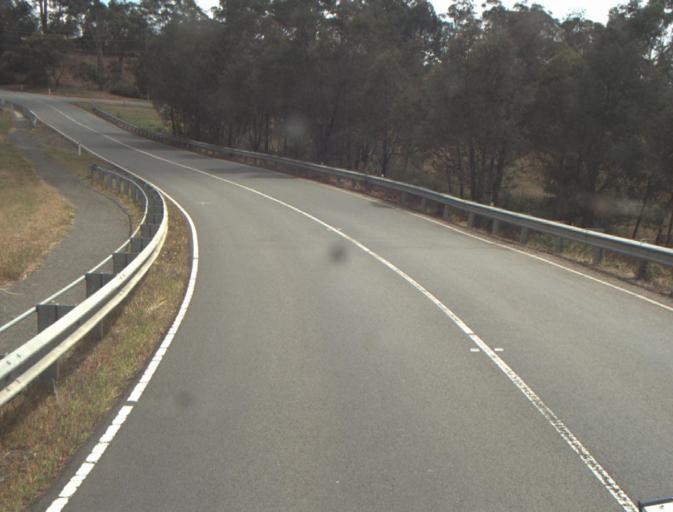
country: AU
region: Tasmania
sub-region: Launceston
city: Newstead
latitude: -41.4745
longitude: 147.1817
